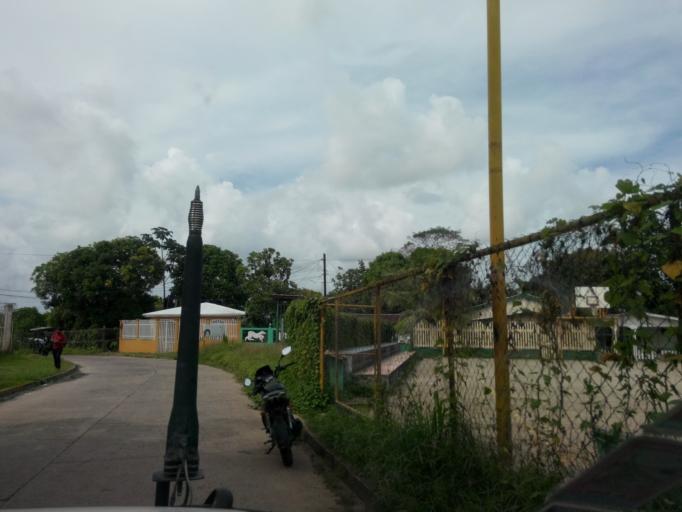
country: NI
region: Atlantico Sur
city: Bluefields
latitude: 12.0027
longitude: -83.7660
